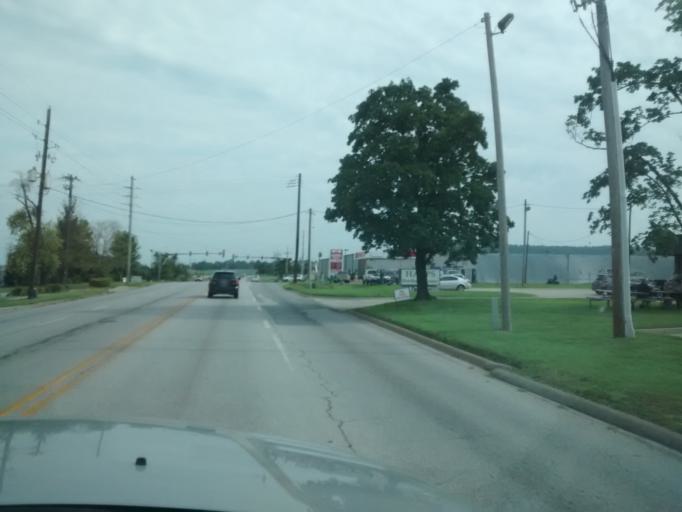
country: US
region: Arkansas
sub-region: Washington County
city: Springdale
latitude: 36.1904
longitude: -94.1162
